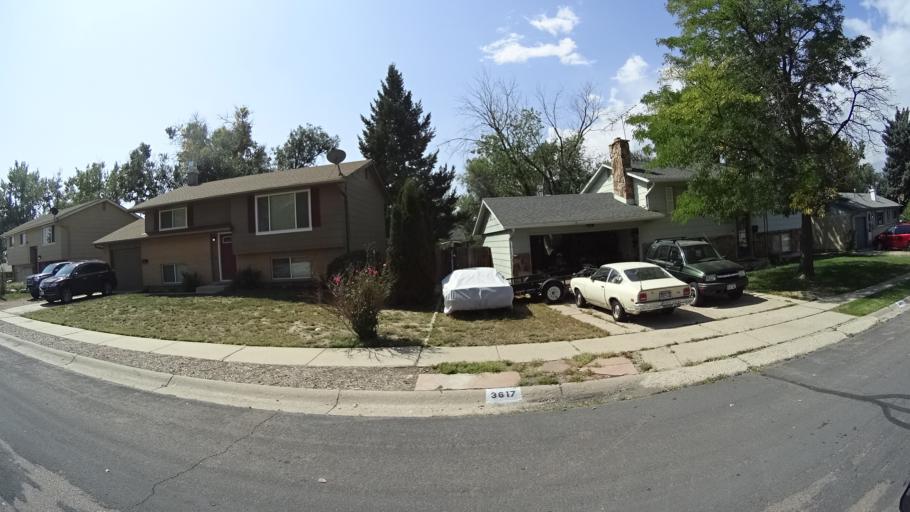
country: US
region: Colorado
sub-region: El Paso County
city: Colorado Springs
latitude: 38.8300
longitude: -104.7652
